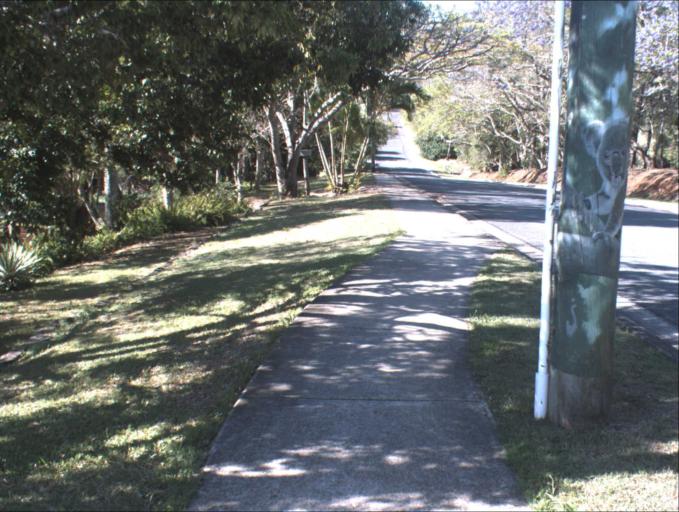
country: AU
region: Queensland
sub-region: Logan
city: Slacks Creek
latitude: -27.6274
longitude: 153.1563
